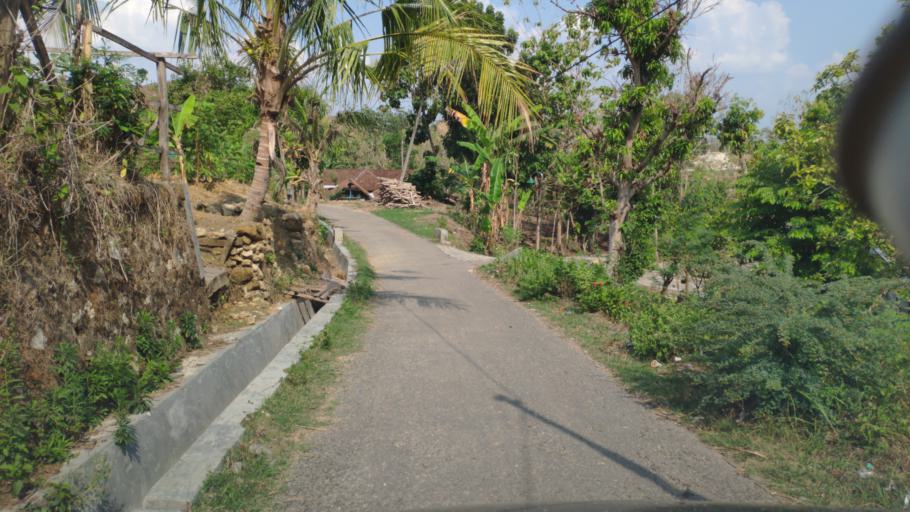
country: ID
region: Central Java
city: Semanggi
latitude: -7.0594
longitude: 111.4287
